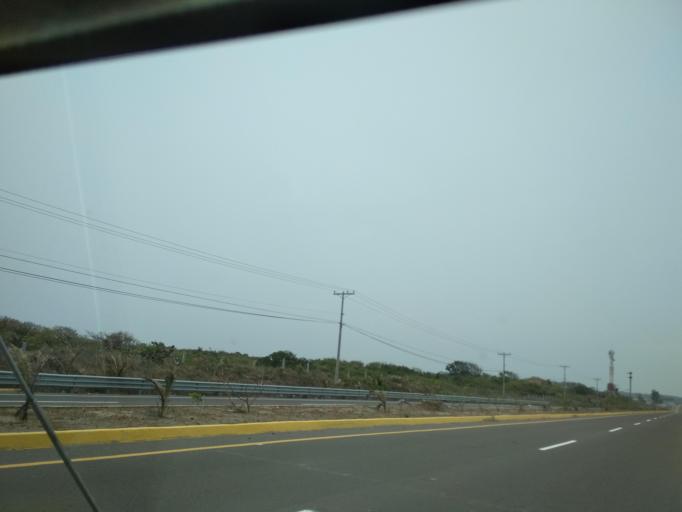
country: MX
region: Veracruz
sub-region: Alvarado
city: Playa de la Libertad
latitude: 19.0557
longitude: -96.0509
